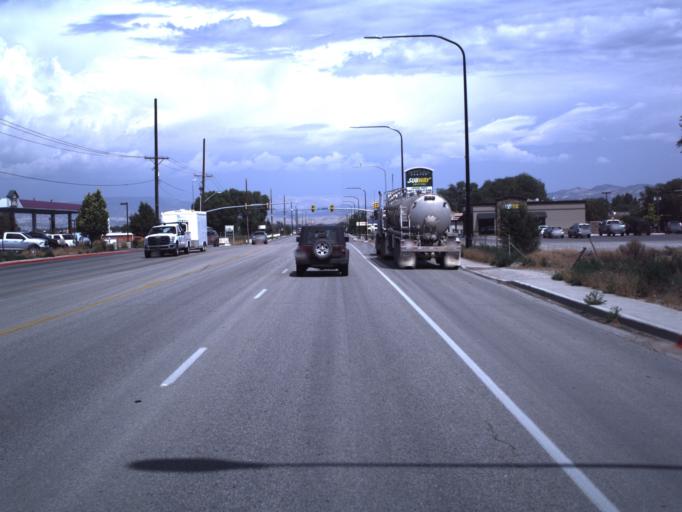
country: US
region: Utah
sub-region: Uintah County
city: Naples
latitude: 40.4179
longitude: -109.4992
